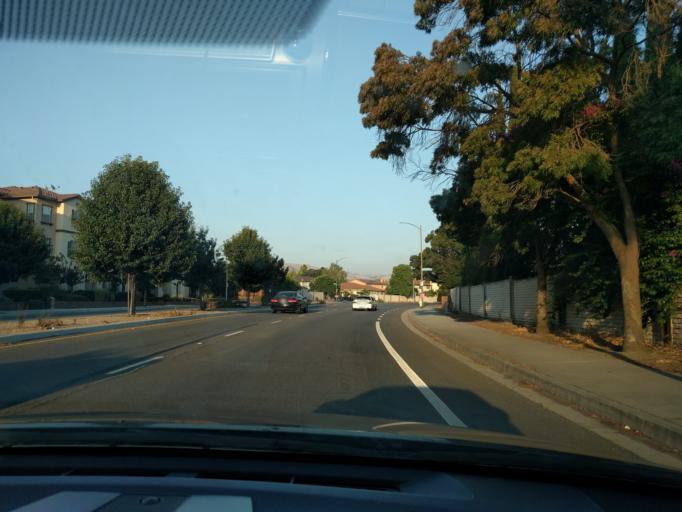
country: US
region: California
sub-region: Santa Clara County
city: Alum Rock
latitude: 37.3790
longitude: -121.8651
